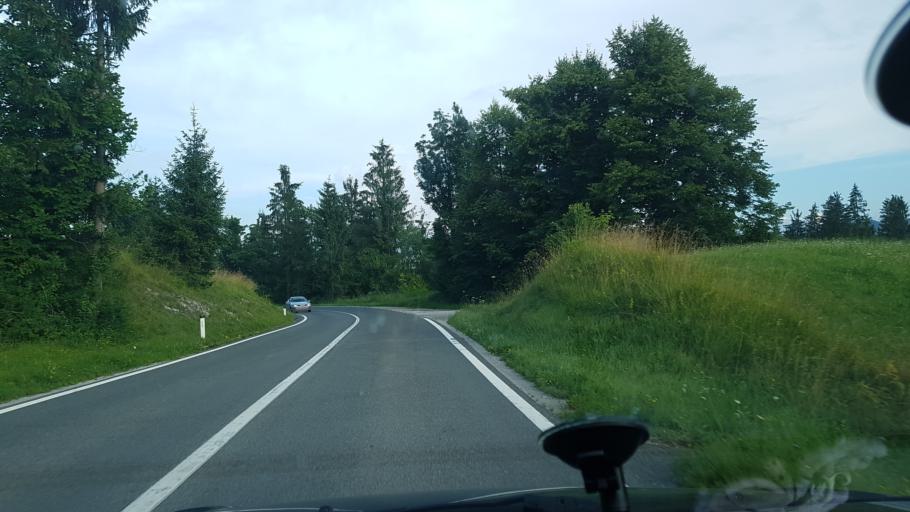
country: SI
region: Idrija
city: Idrija
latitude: 45.9518
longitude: 14.1045
